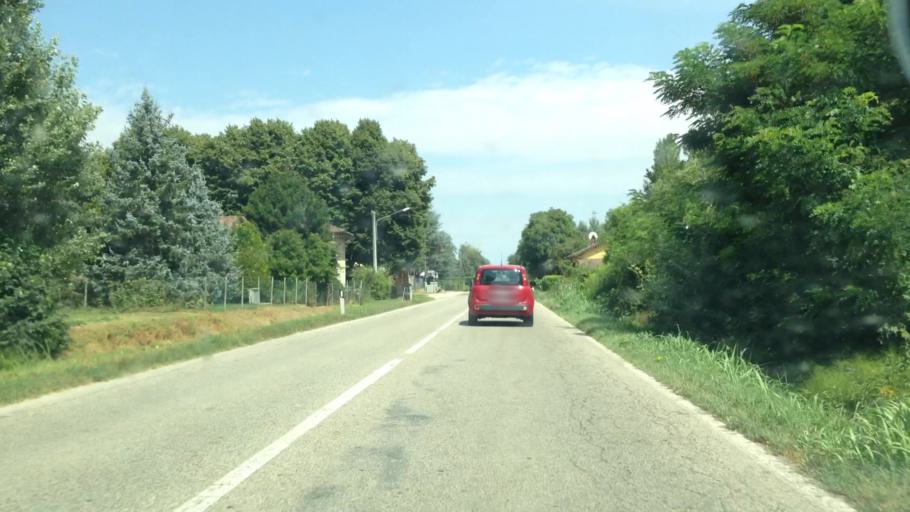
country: IT
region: Piedmont
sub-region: Provincia di Asti
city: Asti
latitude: 44.9279
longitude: 8.2257
